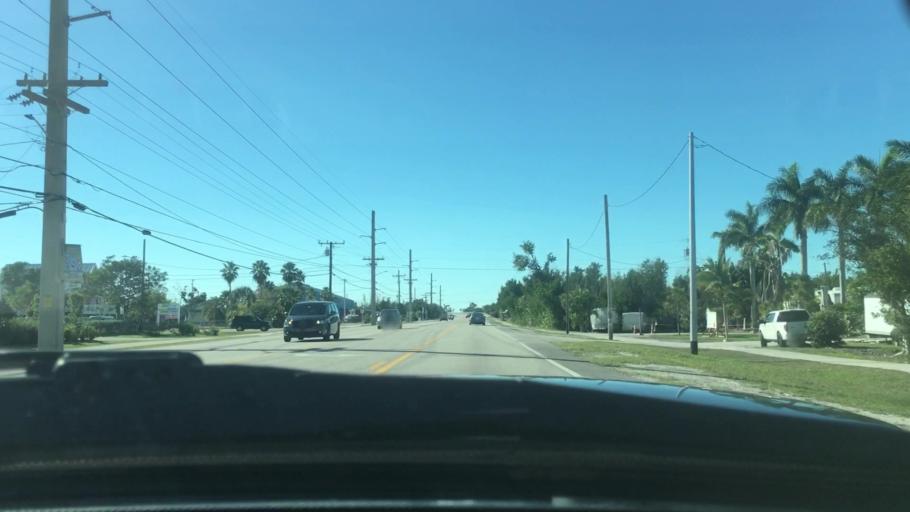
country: US
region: Florida
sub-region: Monroe County
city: Big Pine Key
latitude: 24.6699
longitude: -81.3654
